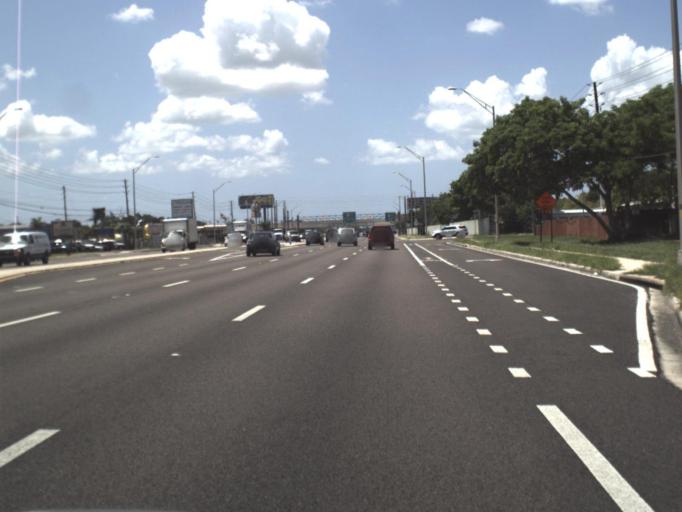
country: US
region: Florida
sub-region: Pinellas County
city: South Highpoint
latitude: 27.8940
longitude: -82.7170
